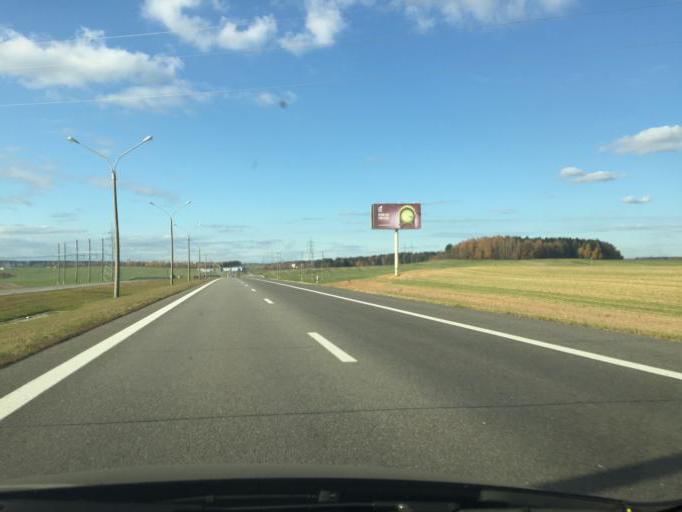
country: BY
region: Minsk
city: Slabada
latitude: 53.9755
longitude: 27.9418
